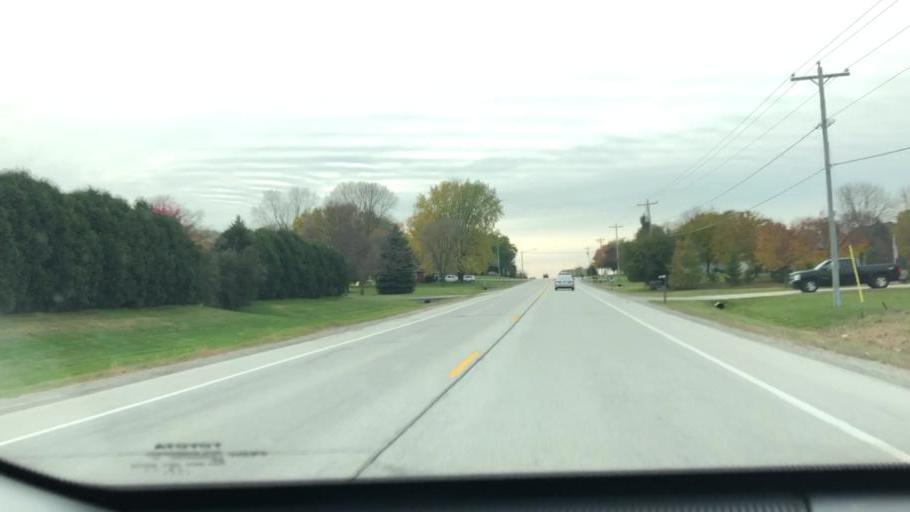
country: US
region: Wisconsin
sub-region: Brown County
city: De Pere
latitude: 44.4452
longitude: -88.1067
